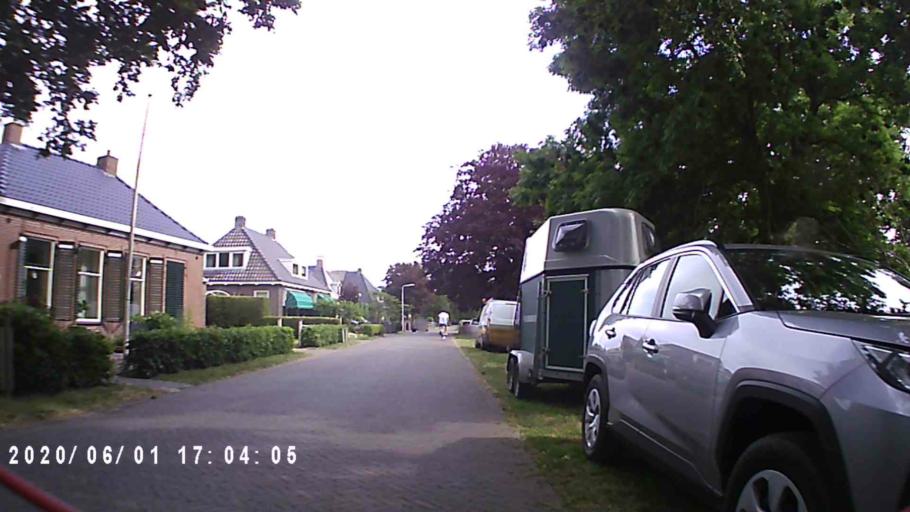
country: NL
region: Friesland
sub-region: Gemeente Tytsjerksteradiel
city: Garyp
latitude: 53.1754
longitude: 5.9328
